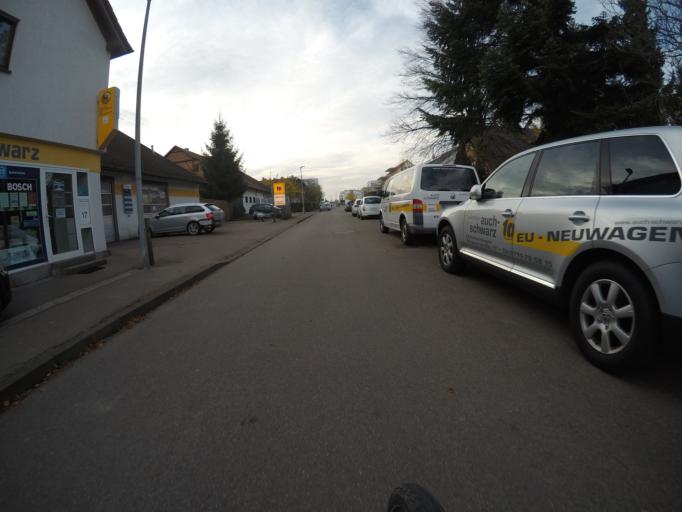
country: DE
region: Baden-Wuerttemberg
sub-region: Regierungsbezirk Stuttgart
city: Leinfelden-Echterdingen
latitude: 48.6939
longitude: 9.1657
